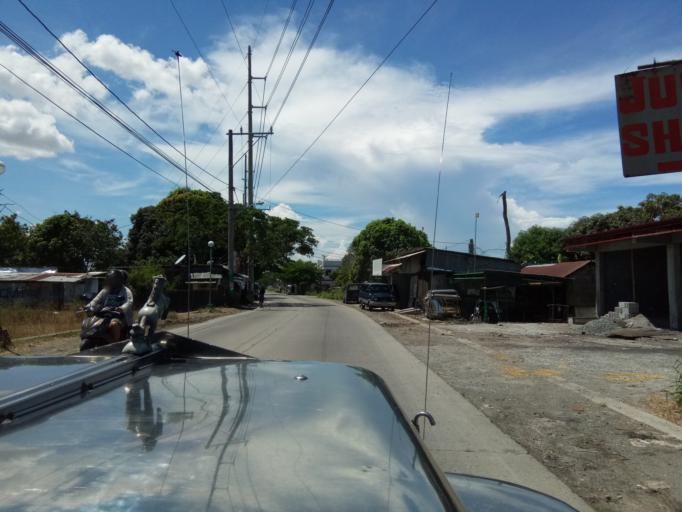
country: PH
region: Calabarzon
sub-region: Province of Cavite
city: Dasmarinas
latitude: 14.3281
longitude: 120.9116
